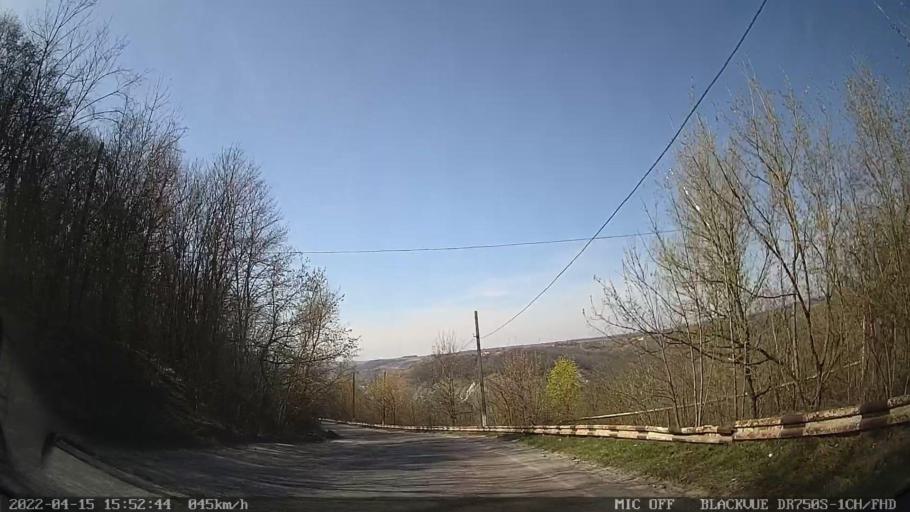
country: MD
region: Raionul Ocnita
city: Otaci
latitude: 48.3960
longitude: 27.8909
